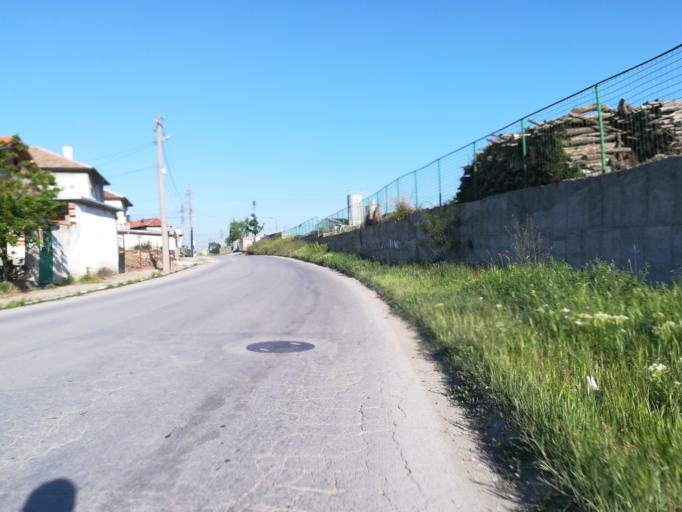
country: BG
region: Stara Zagora
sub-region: Obshtina Chirpan
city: Chirpan
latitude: 42.1075
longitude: 25.2268
